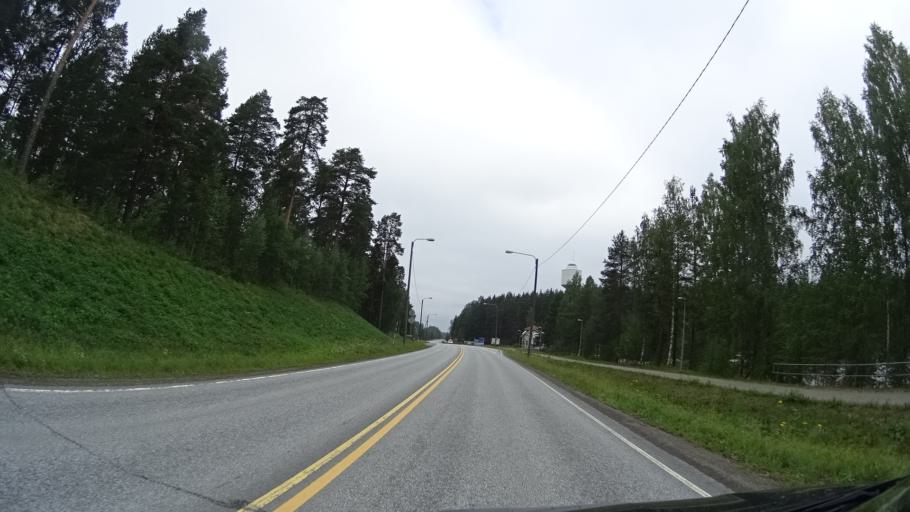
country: FI
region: Southern Savonia
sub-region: Savonlinna
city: Punkaharju
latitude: 61.7609
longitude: 29.3859
